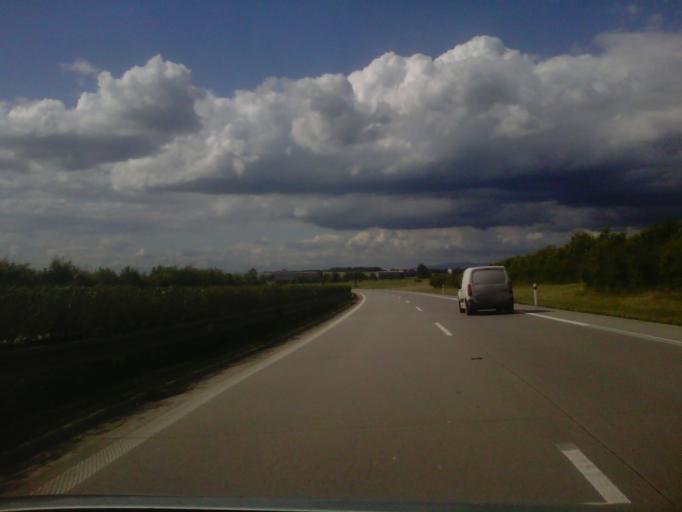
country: CZ
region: Olomoucky
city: Hnevotin
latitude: 49.5813
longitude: 17.2075
